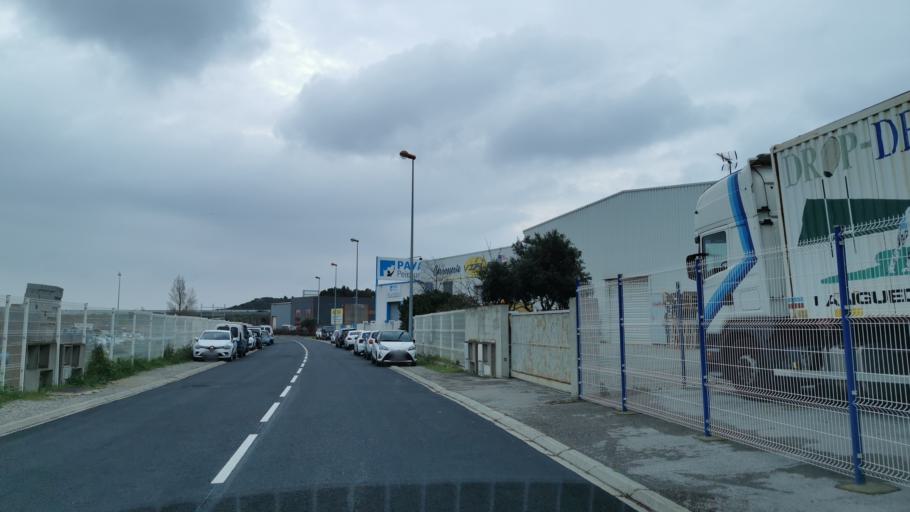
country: FR
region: Languedoc-Roussillon
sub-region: Departement de l'Aude
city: Narbonne
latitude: 43.1543
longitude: 2.9820
